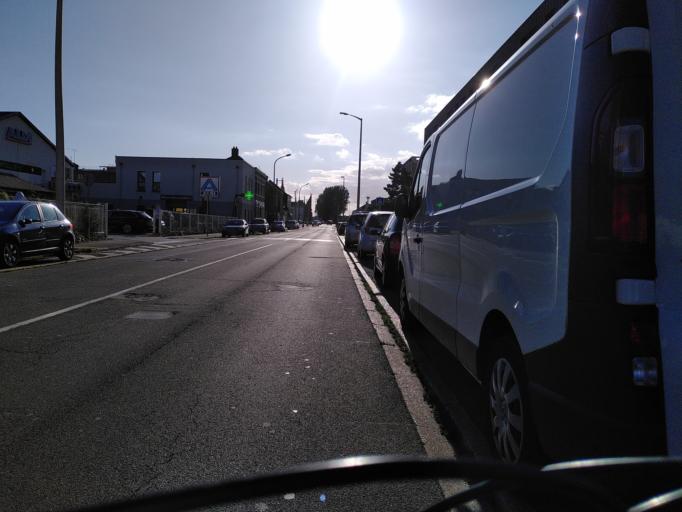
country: FR
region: Nord-Pas-de-Calais
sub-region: Departement du Pas-de-Calais
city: Calais
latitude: 50.9563
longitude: 1.8666
